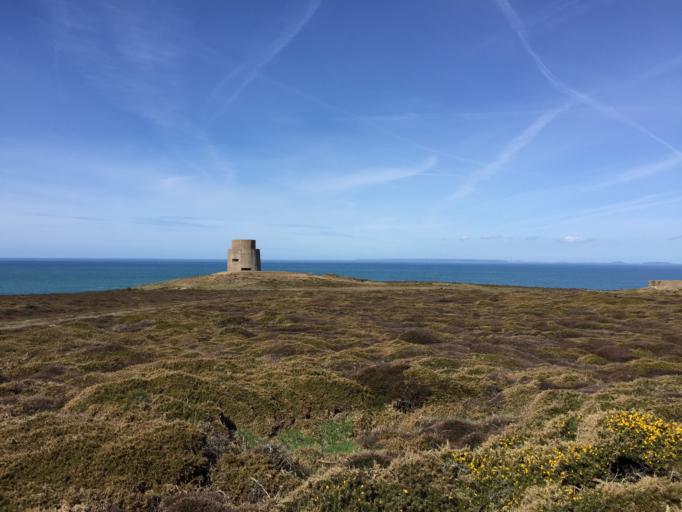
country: JE
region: St Helier
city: Saint Helier
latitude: 49.2516
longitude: -2.2508
